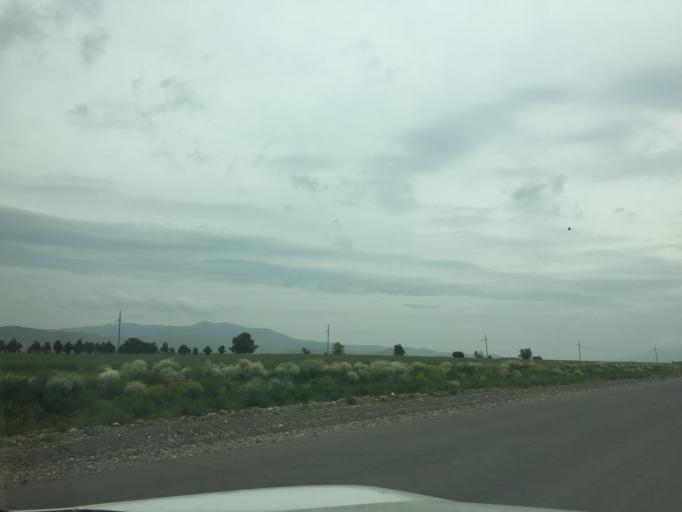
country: KZ
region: Ongtustik Qazaqstan
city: Turar Ryskulov
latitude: 42.5103
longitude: 70.3935
